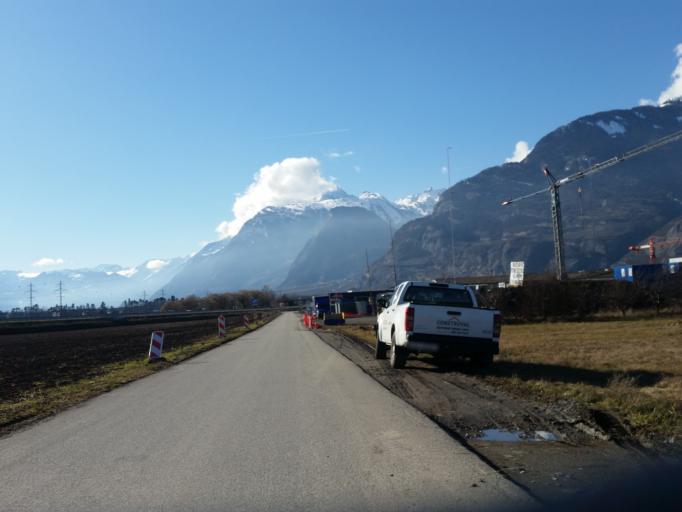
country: CH
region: Valais
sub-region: Conthey District
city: Conthey
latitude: 46.2139
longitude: 7.3004
